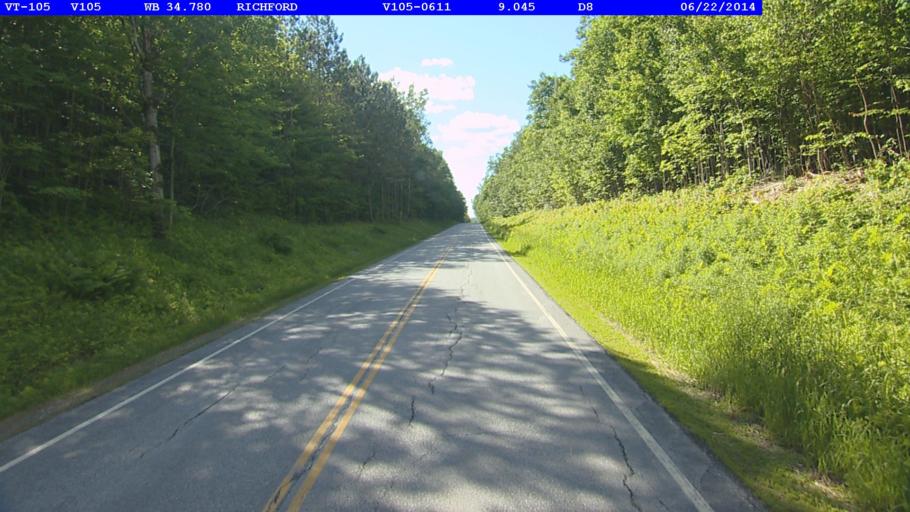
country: US
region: Vermont
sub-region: Franklin County
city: Richford
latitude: 44.9871
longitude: -72.5527
